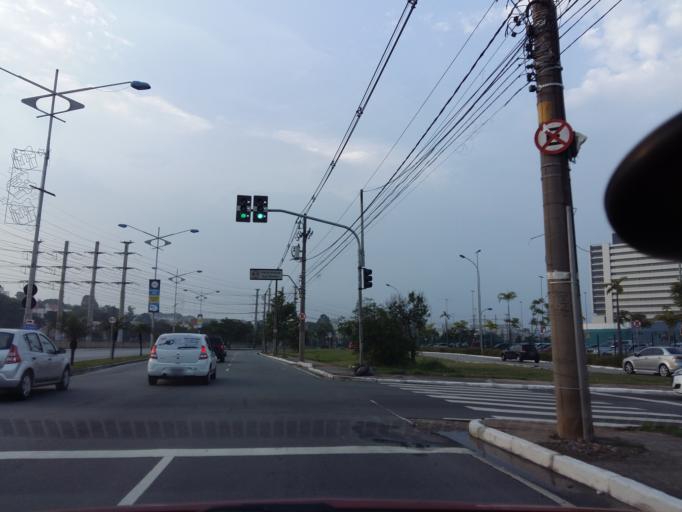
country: BR
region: Sao Paulo
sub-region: Sao Caetano Do Sul
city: Sao Caetano do Sul
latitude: -23.6275
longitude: -46.5813
